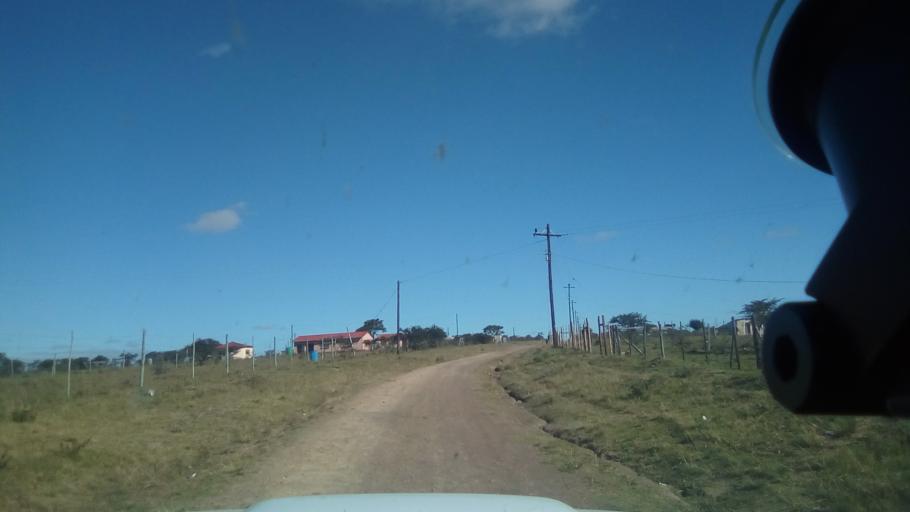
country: ZA
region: Eastern Cape
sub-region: Buffalo City Metropolitan Municipality
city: Bhisho
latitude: -32.7815
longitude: 27.3366
